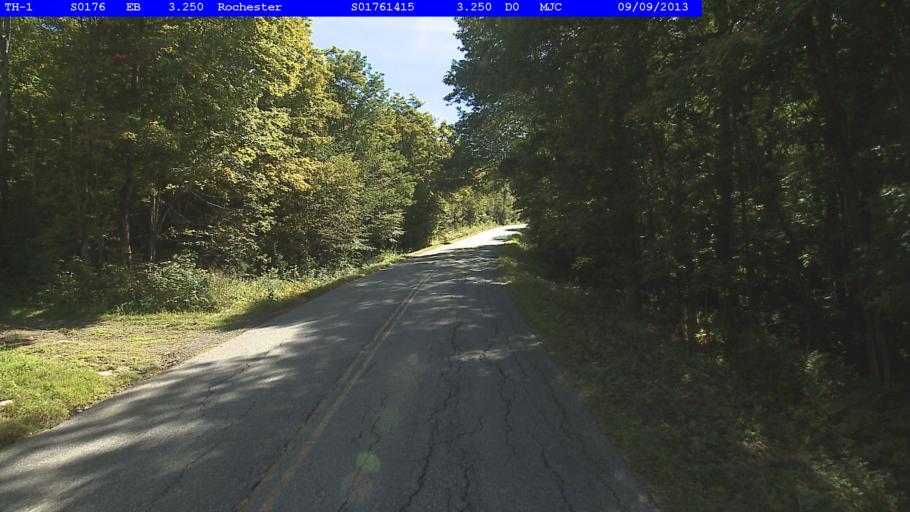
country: US
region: Vermont
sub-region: Orange County
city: Randolph
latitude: 43.8589
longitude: -72.7597
